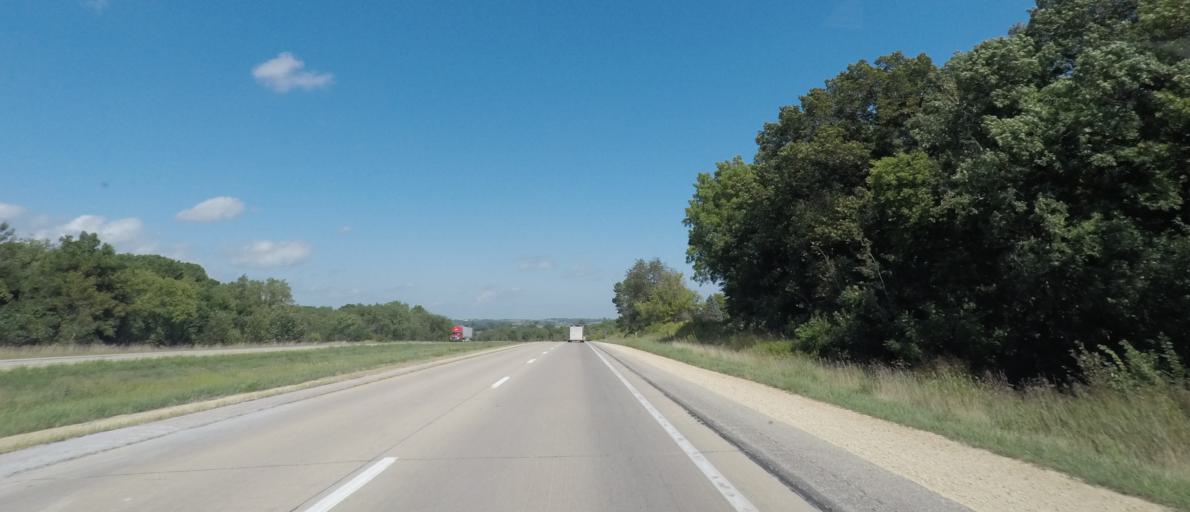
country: US
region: Iowa
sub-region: Jones County
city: Anamosa
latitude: 42.0775
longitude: -91.2790
